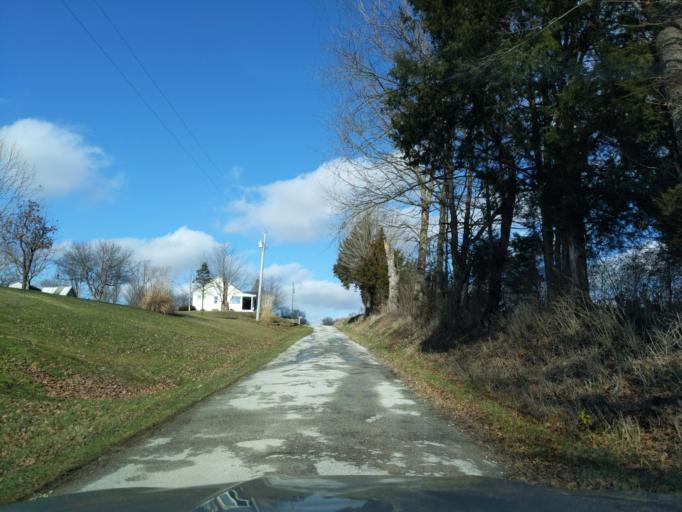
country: US
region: Indiana
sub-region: Decatur County
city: Greensburg
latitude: 39.2541
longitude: -85.4842
